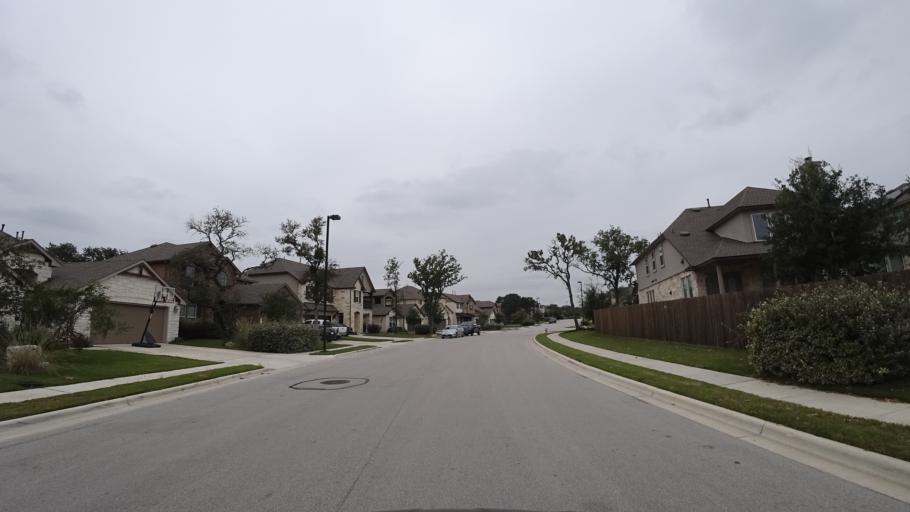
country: US
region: Texas
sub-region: Travis County
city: Shady Hollow
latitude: 30.1814
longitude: -97.9068
